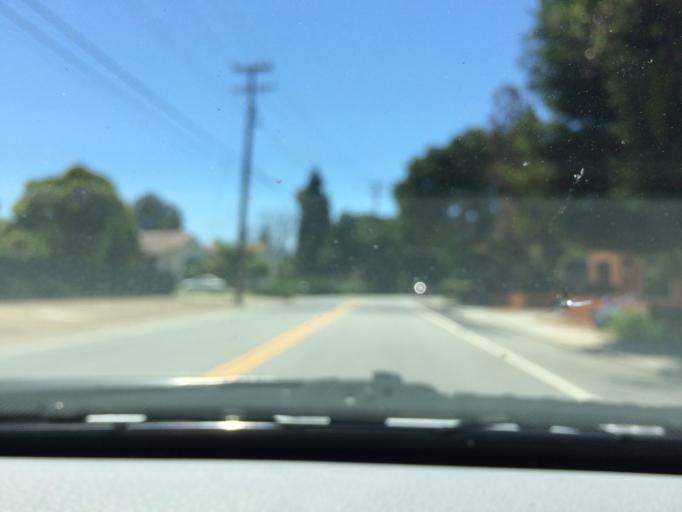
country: US
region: California
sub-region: San Mateo County
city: East Palo Alto
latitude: 37.4695
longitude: -122.1587
